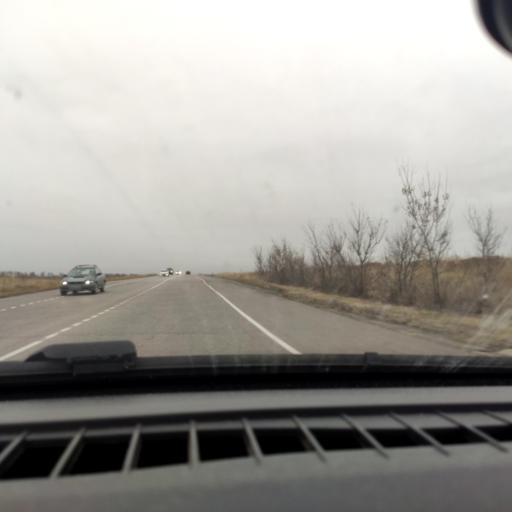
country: RU
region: Voronezj
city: Devitsa
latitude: 51.5794
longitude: 38.9755
